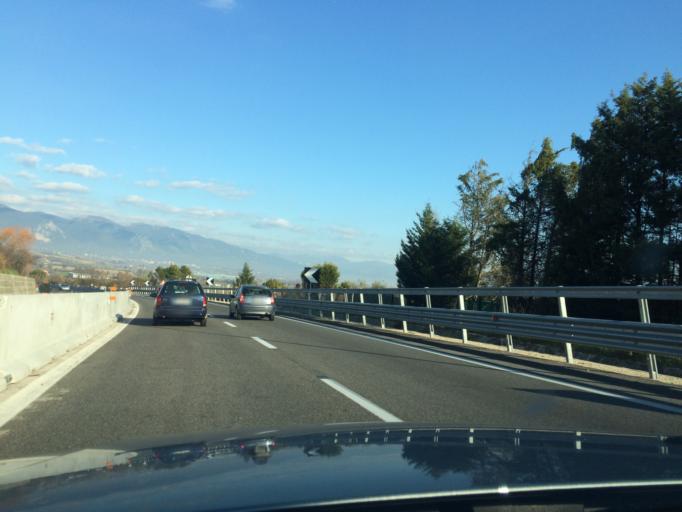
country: IT
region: Umbria
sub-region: Provincia di Terni
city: Narni Scalo
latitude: 42.5411
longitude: 12.5157
